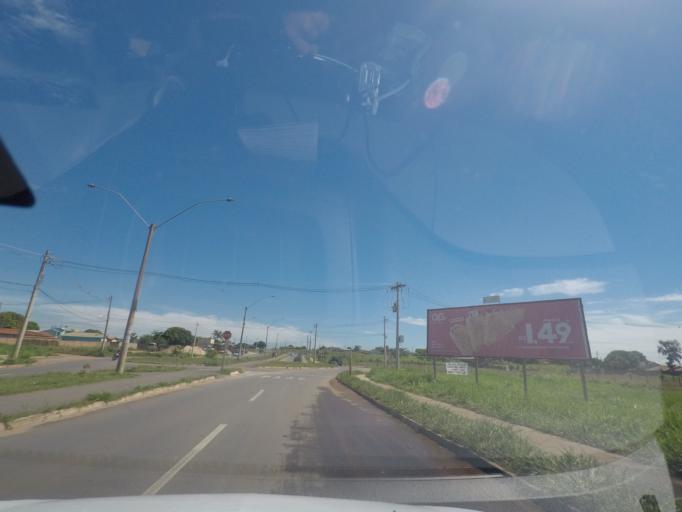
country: BR
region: Goias
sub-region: Aparecida De Goiania
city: Aparecida de Goiania
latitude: -16.7969
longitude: -49.3289
